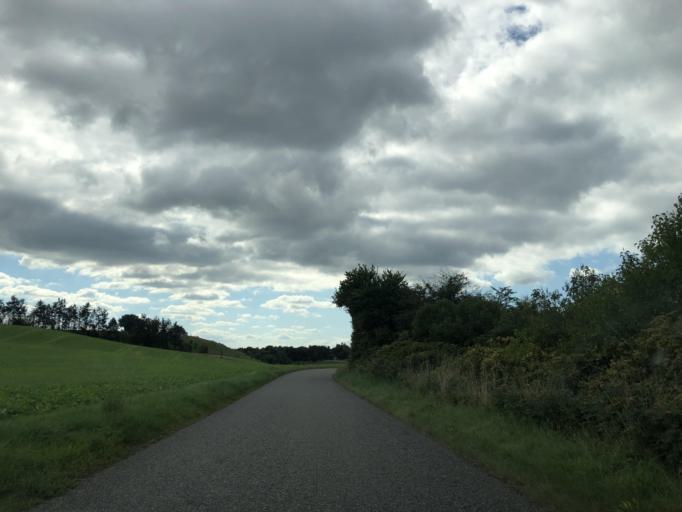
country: DK
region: Central Jutland
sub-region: Viborg Kommune
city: Viborg
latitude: 56.5877
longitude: 9.4003
